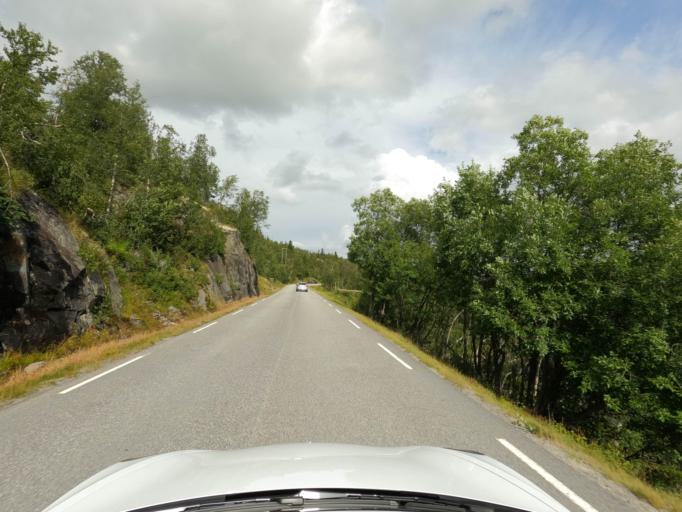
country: NO
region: Telemark
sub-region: Tinn
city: Rjukan
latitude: 59.8446
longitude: 8.4157
